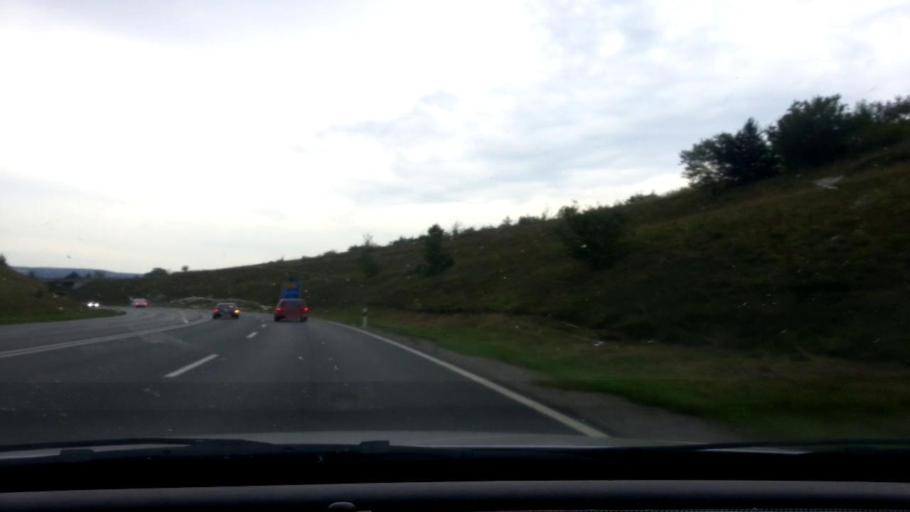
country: DE
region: Bavaria
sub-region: Upper Franconia
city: Bayreuth
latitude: 49.9250
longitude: 11.6050
